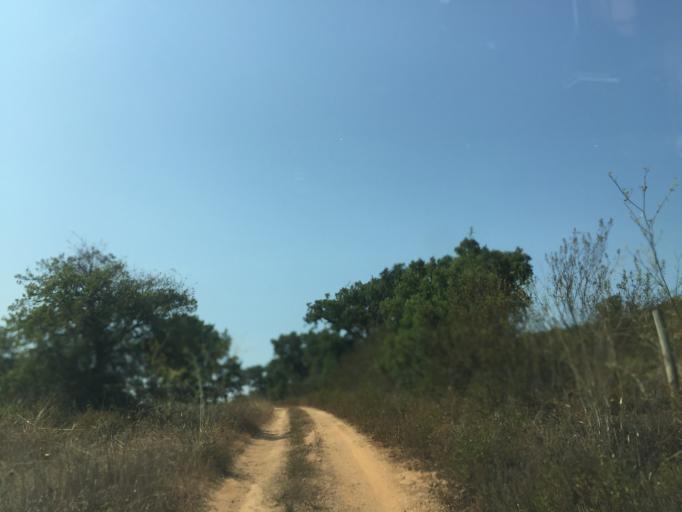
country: PT
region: Setubal
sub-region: Santiago do Cacem
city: Santiago do Cacem
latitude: 37.9728
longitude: -8.5152
